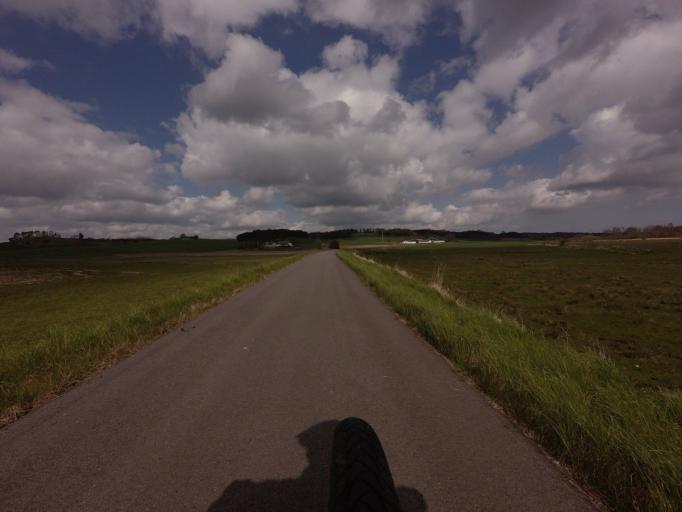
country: DK
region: North Denmark
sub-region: Mariagerfjord Kommune
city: Hadsund
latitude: 56.8486
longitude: 10.0980
